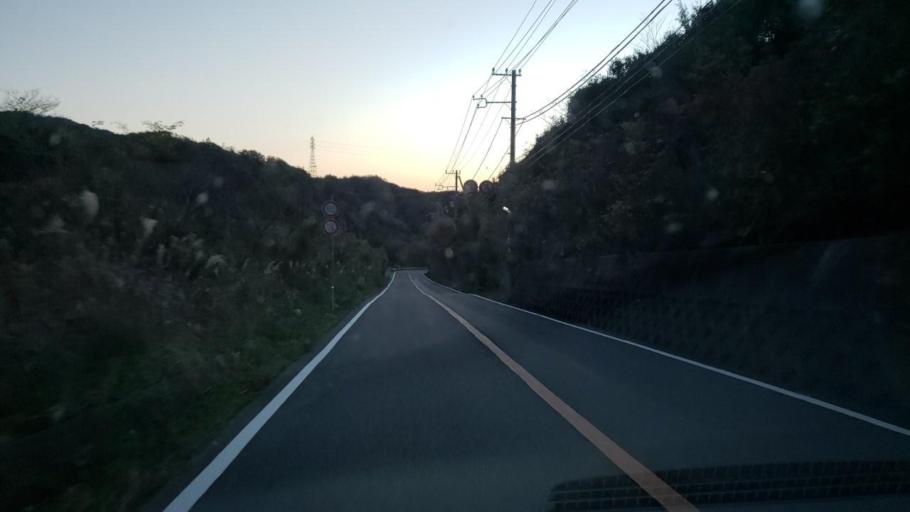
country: JP
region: Hyogo
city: Fukura
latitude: 34.2806
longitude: 134.7043
